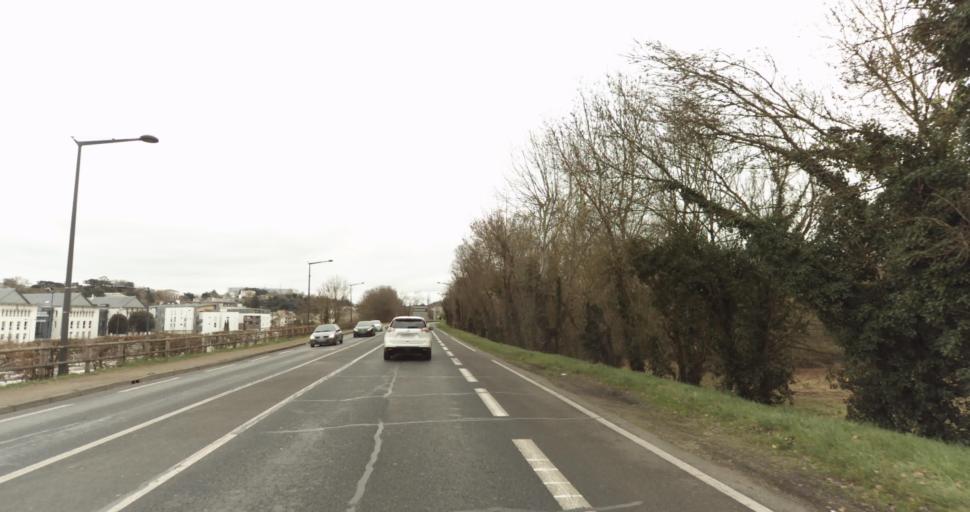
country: FR
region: Pays de la Loire
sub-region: Departement de Maine-et-Loire
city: Saumur
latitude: 47.2518
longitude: -0.0818
